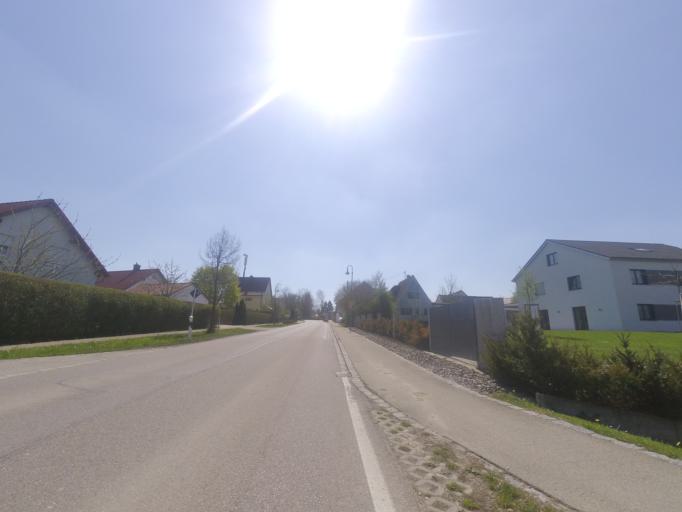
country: DE
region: Bavaria
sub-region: Swabia
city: Roggenburg
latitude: 48.2794
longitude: 10.2299
